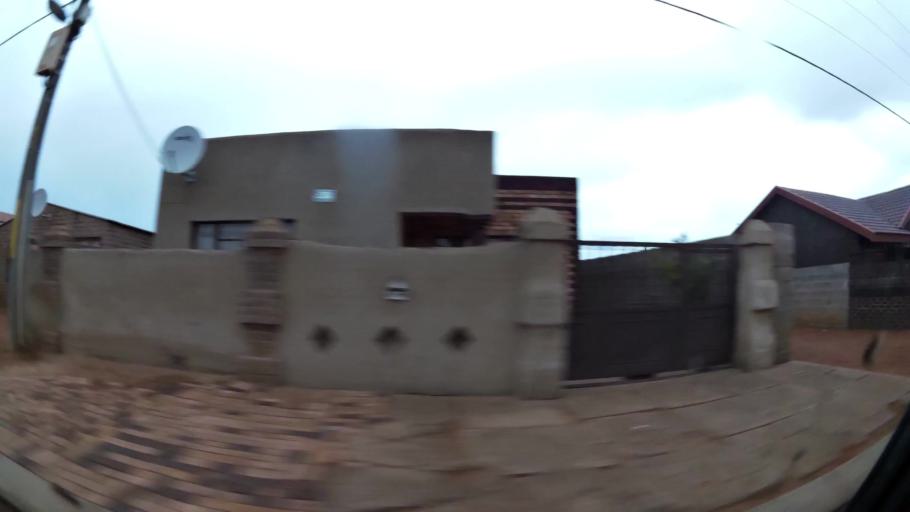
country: ZA
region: Gauteng
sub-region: City of Johannesburg Metropolitan Municipality
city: Roodepoort
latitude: -26.1748
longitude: 27.7877
